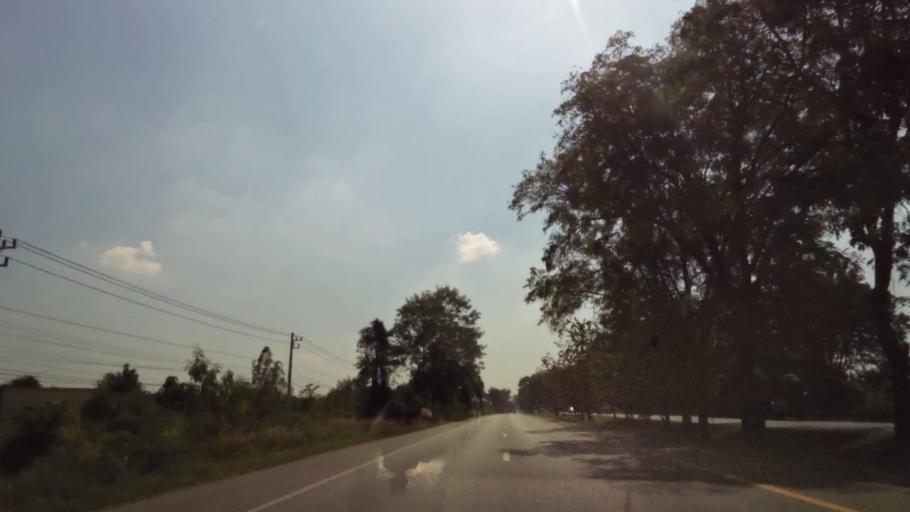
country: TH
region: Phichit
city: Bueng Na Rang
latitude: 16.1799
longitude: 100.1284
